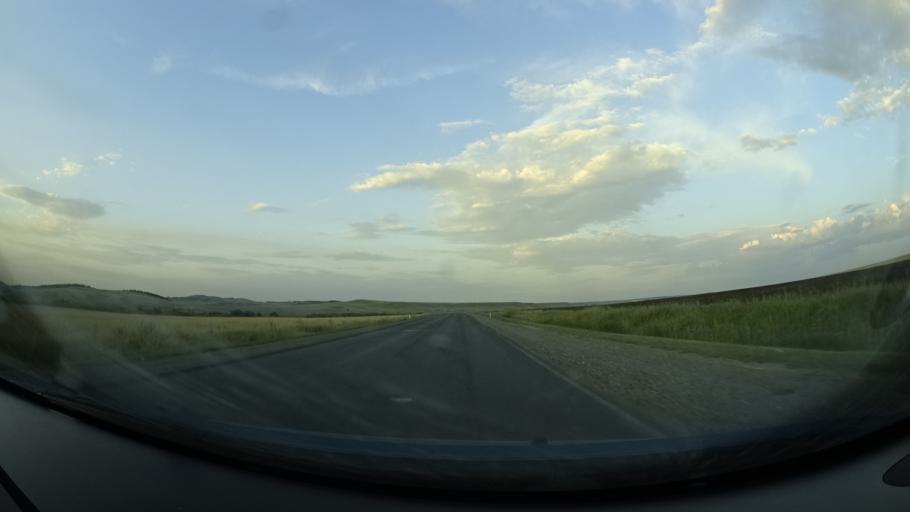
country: RU
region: Orenburg
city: Severnoye
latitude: 54.1277
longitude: 52.5729
